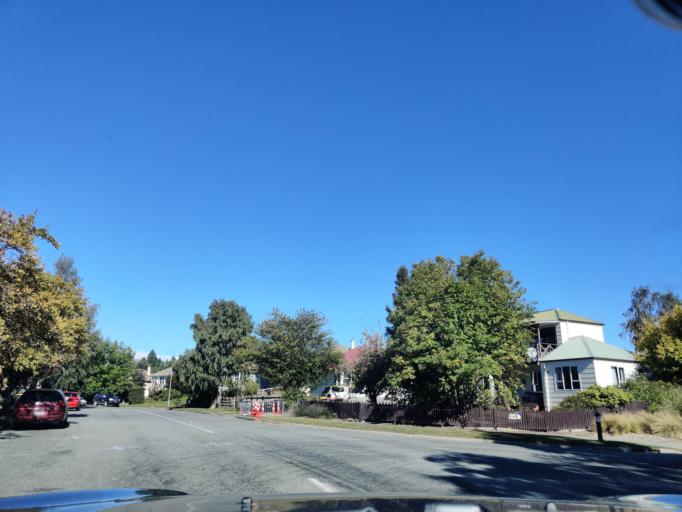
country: NZ
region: Canterbury
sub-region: Timaru District
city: Pleasant Point
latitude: -44.0066
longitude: 170.4751
